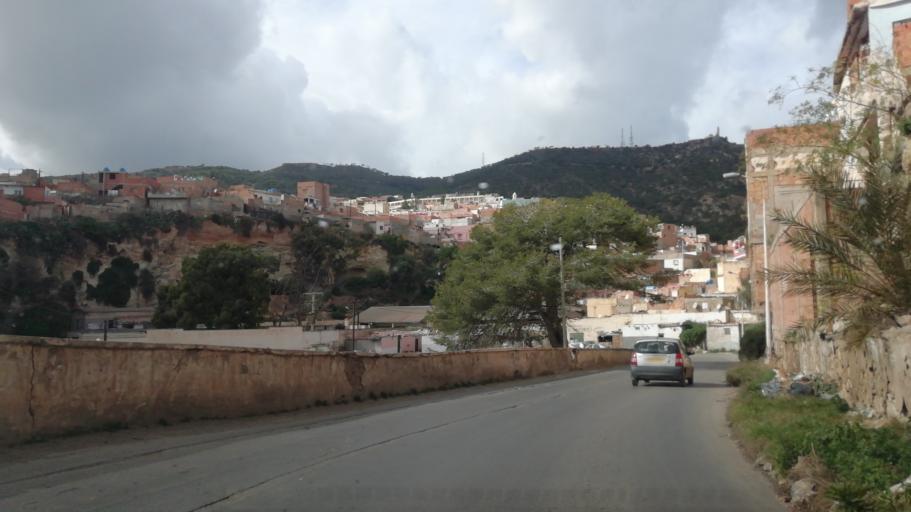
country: DZ
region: Oran
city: Oran
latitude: 35.6980
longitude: -0.6609
